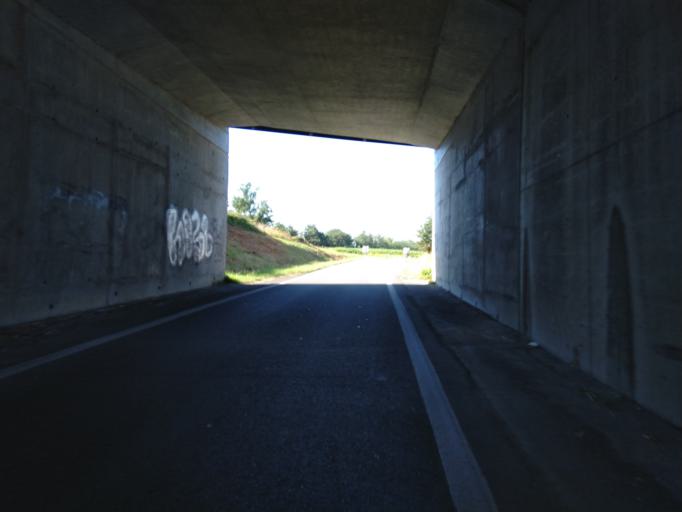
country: FR
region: Aquitaine
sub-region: Departement des Landes
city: Saint-Vincent-de-Paul
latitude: 43.7372
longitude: -1.0263
